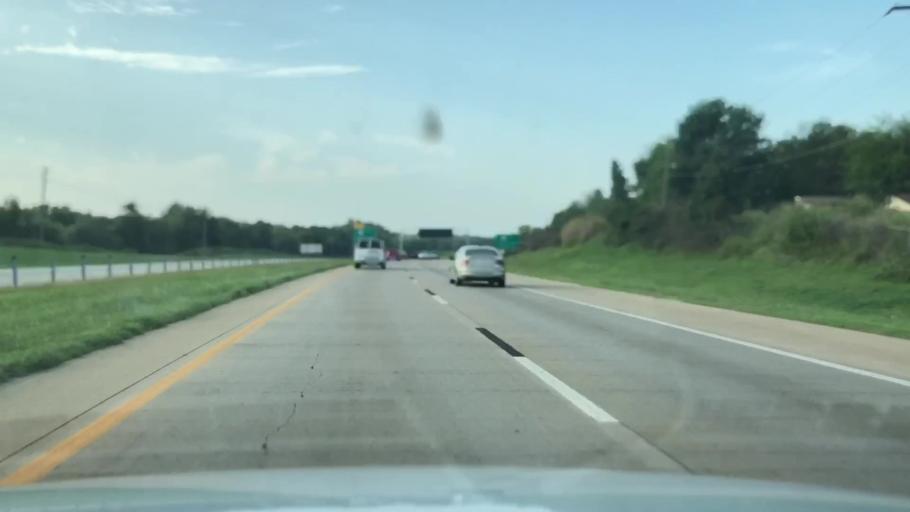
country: US
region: Oklahoma
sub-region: Tulsa County
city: Turley
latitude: 36.2187
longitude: -95.9448
